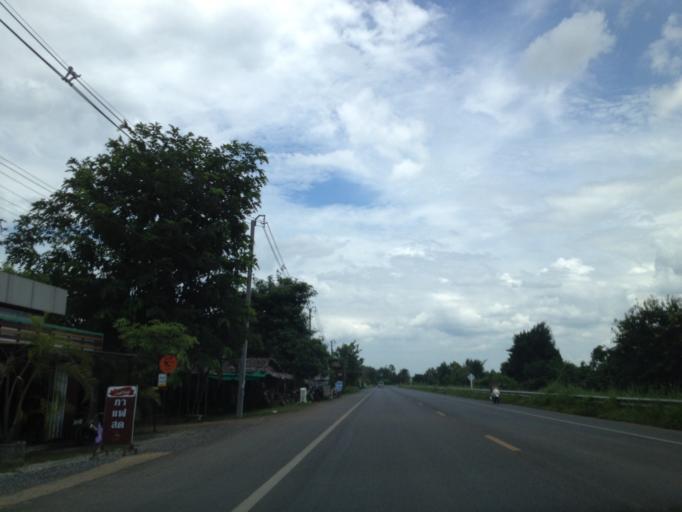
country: TH
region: Chiang Mai
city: San Pa Tong
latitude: 18.6326
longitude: 98.8721
